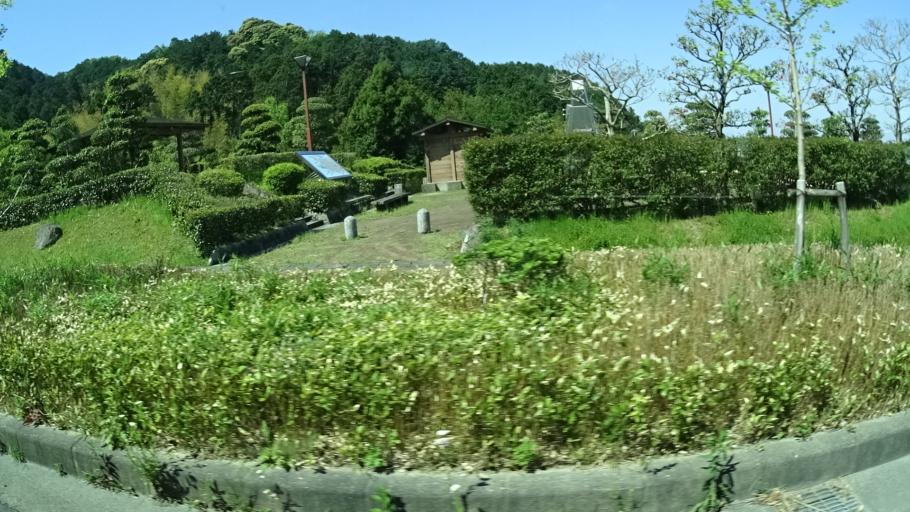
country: JP
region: Mie
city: Toba
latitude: 34.5033
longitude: 136.7810
